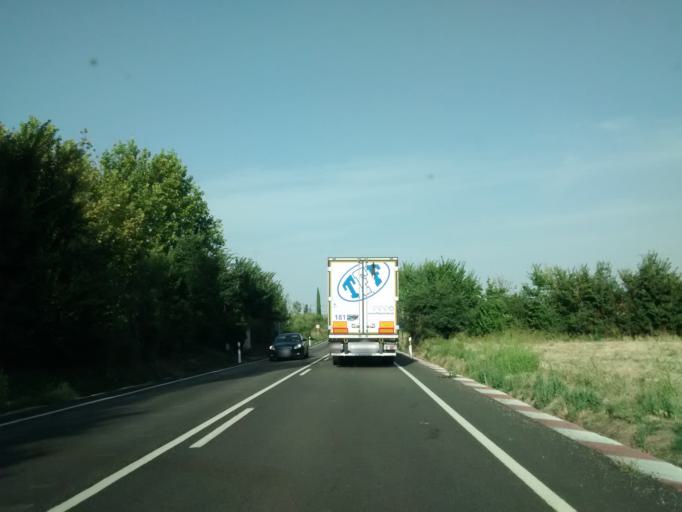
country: ES
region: Aragon
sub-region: Provincia de Zaragoza
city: Malejan
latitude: 41.8297
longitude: -1.5426
